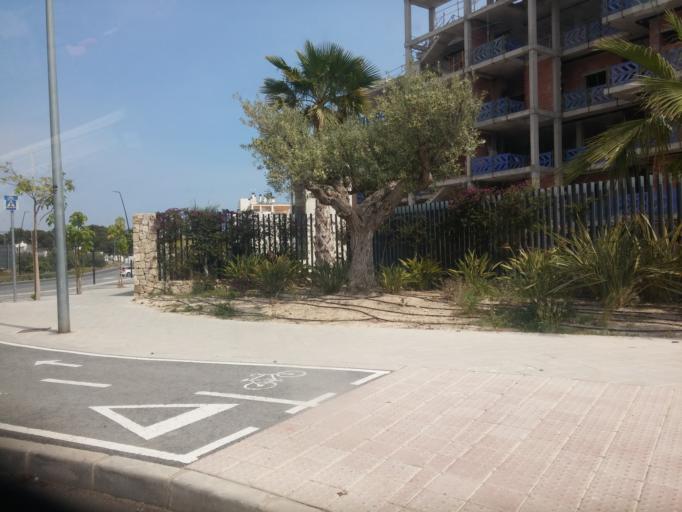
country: ES
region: Valencia
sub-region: Provincia de Alicante
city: Villajoyosa
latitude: 38.4986
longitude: -0.2582
